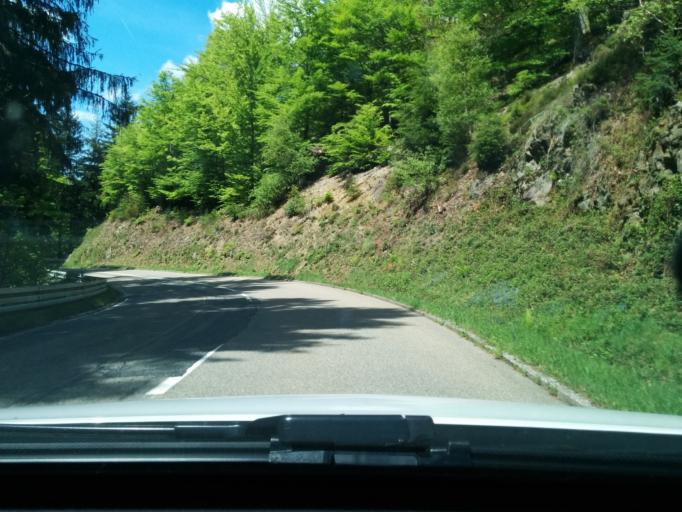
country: DE
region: Baden-Wuerttemberg
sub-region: Freiburg Region
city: Horben
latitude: 47.9225
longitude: 7.8768
